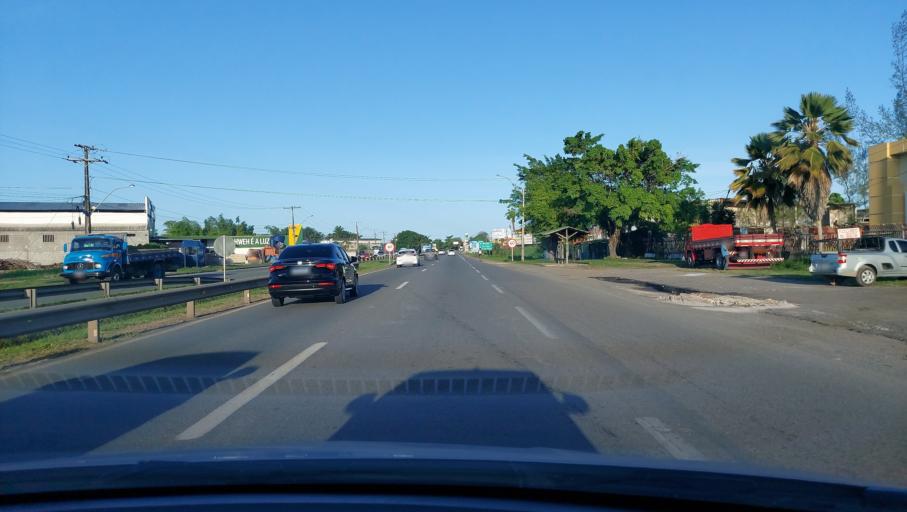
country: BR
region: Bahia
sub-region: Lauro De Freitas
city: Lauro de Freitas
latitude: -12.8259
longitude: -38.2604
